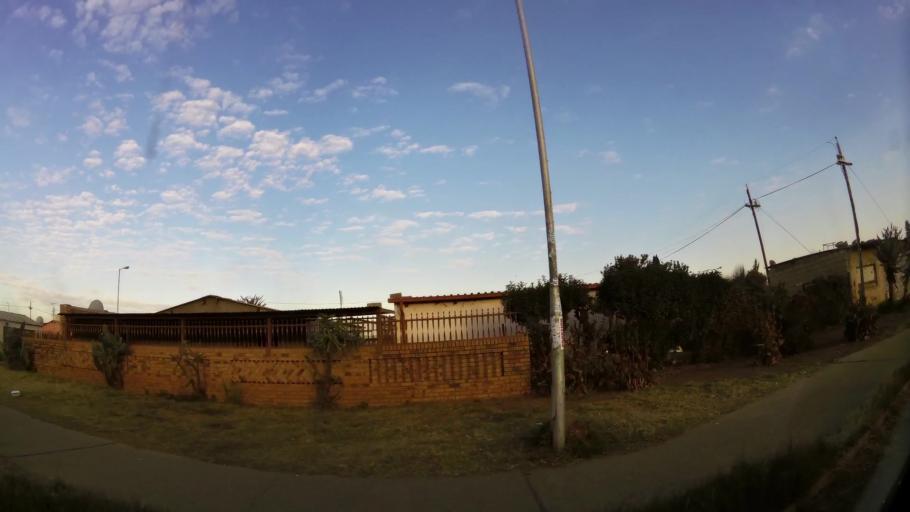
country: ZA
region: Gauteng
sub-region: City of Tshwane Metropolitan Municipality
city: Pretoria
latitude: -25.7135
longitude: 28.3559
